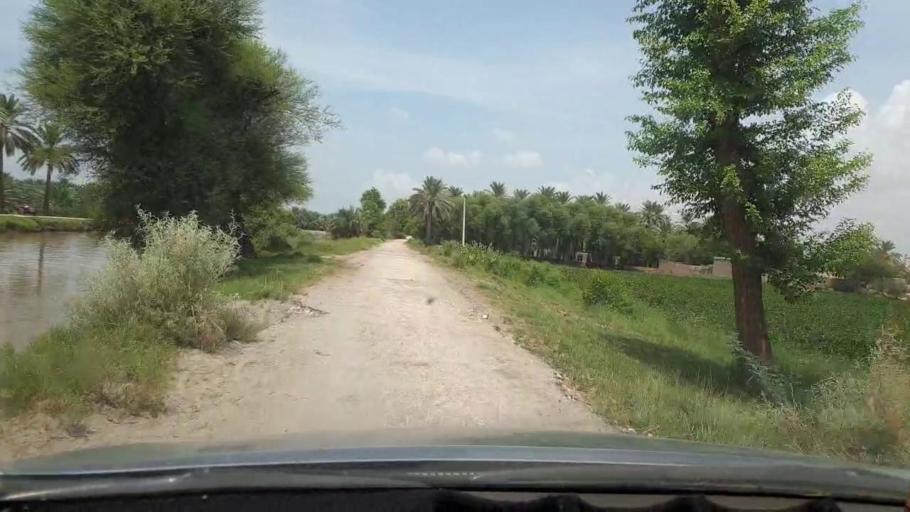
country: PK
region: Sindh
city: Khairpur
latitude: 27.4554
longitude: 68.7998
